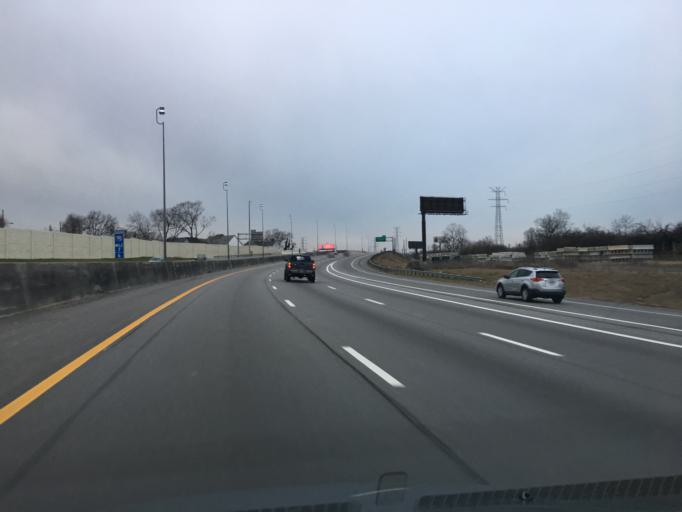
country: US
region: Ohio
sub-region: Hamilton County
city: Saint Bernard
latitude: 39.1725
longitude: -84.4927
